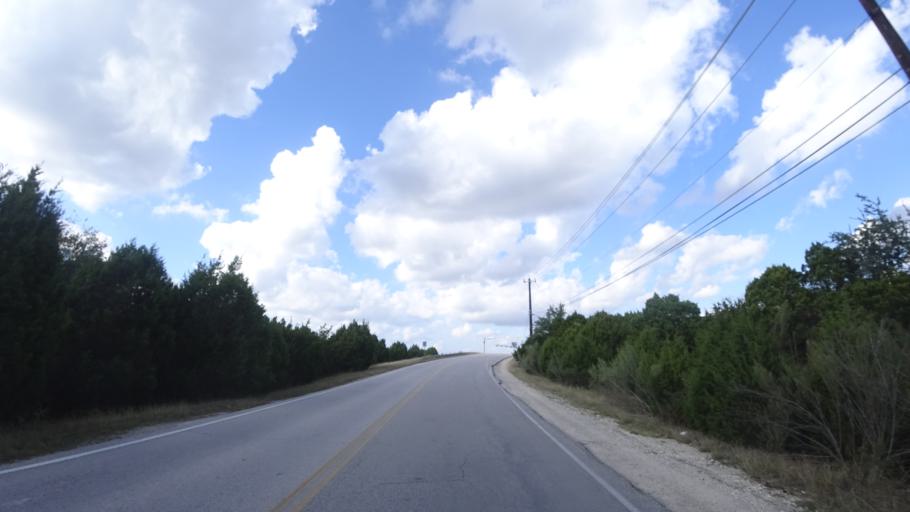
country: US
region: Texas
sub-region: Travis County
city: Barton Creek
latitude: 30.2608
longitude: -97.8886
